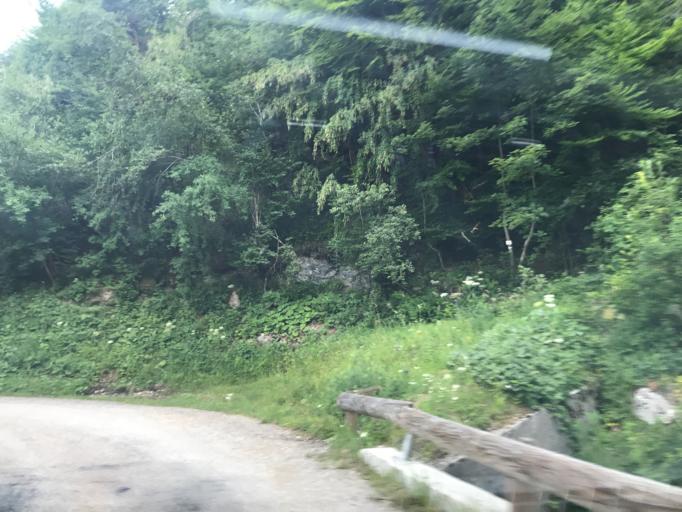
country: FR
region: Rhone-Alpes
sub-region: Departement de l'Isere
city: Saint-Vincent-de-Mercuze
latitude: 45.3805
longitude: 5.9221
